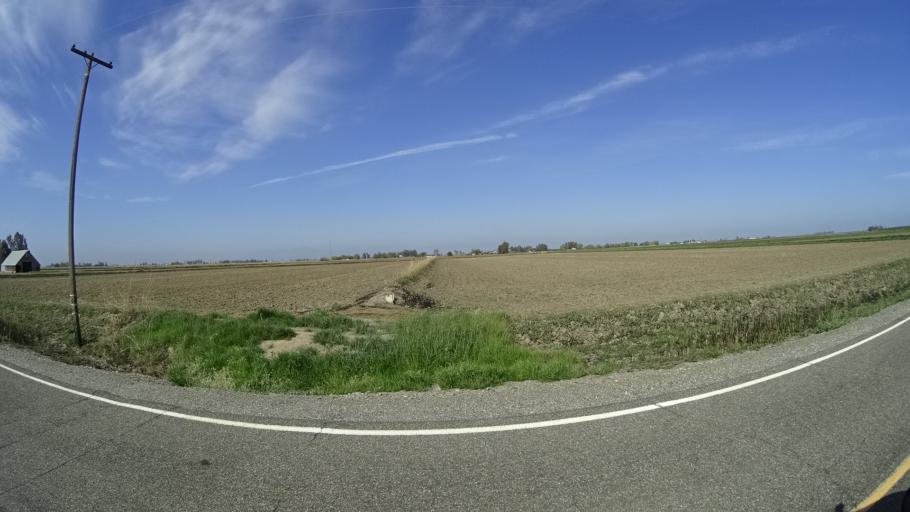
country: US
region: California
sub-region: Glenn County
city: Hamilton City
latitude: 39.5972
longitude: -122.0368
